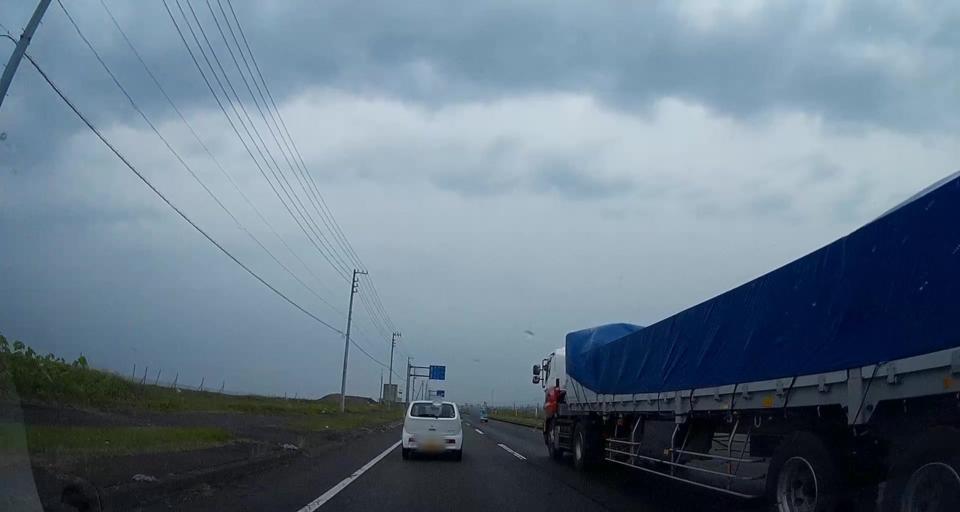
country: JP
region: Hokkaido
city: Shiraoi
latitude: 42.5951
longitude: 141.4678
